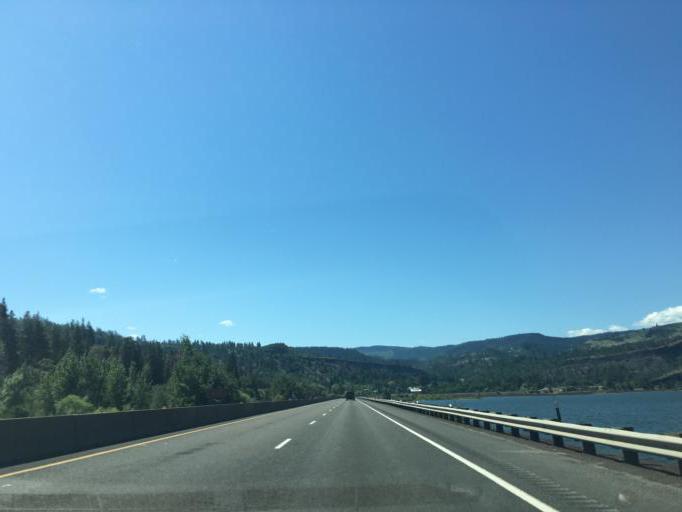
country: US
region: Washington
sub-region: Klickitat County
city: White Salmon
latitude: 45.6909
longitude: -121.3869
